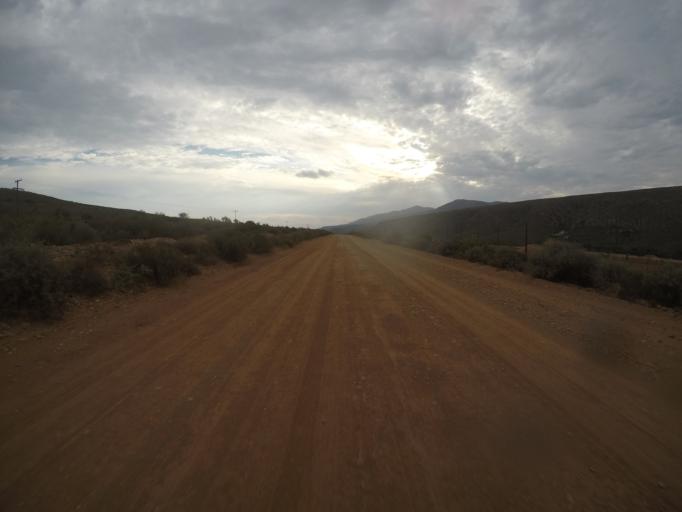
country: ZA
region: Eastern Cape
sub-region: Cacadu District Municipality
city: Willowmore
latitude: -33.4883
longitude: 23.5566
